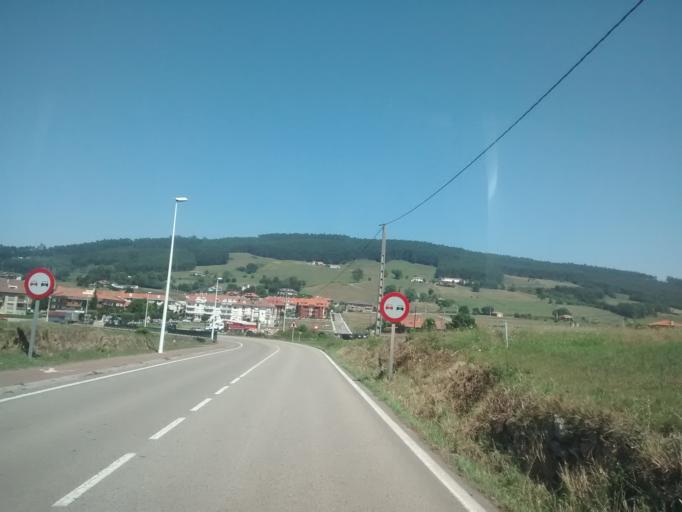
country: ES
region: Cantabria
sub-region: Provincia de Cantabria
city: San Miguel de Meruelo
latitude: 43.4504
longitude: -3.5720
